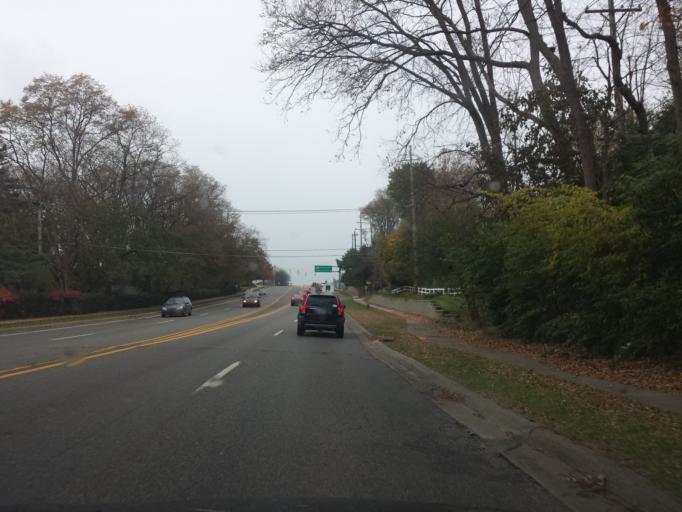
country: US
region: Michigan
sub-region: Oakland County
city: Bingham Farms
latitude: 42.5450
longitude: -83.2795
